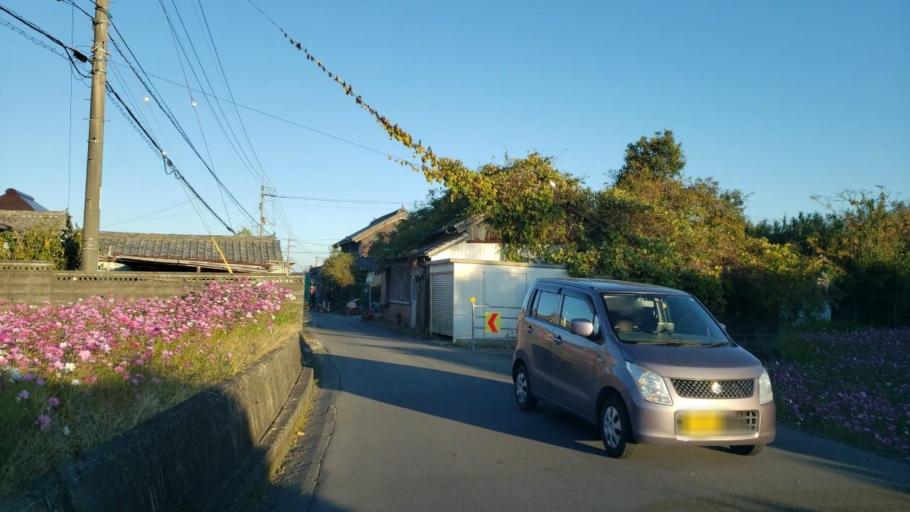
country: JP
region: Tokushima
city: Kamojimacho-jogejima
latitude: 34.1009
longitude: 134.3132
